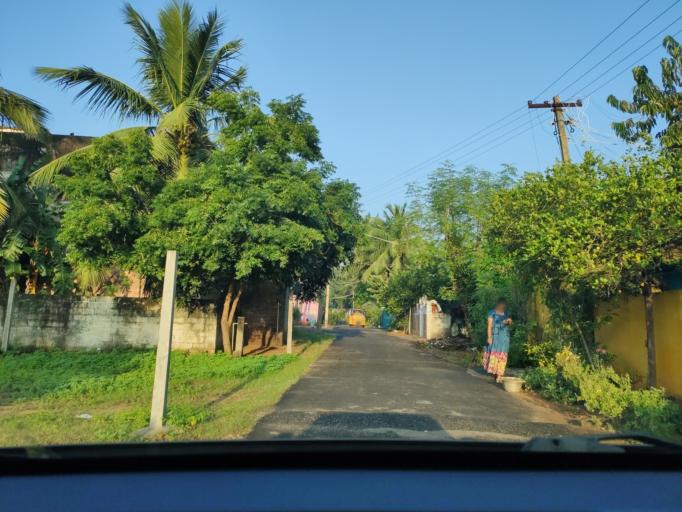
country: IN
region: Tamil Nadu
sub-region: Villupuram
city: Auroville
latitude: 12.0641
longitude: 79.8828
